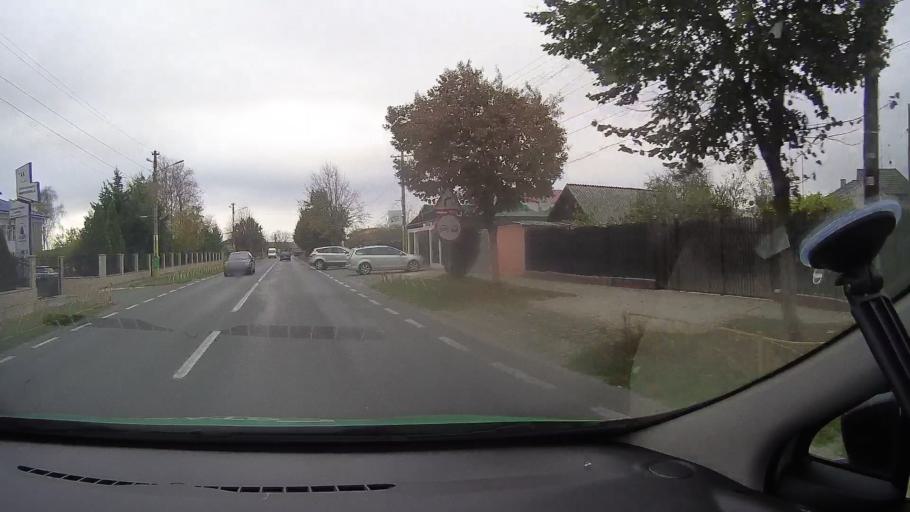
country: RO
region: Constanta
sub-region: Oras Murfatlar
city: Murfatlar
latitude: 44.1755
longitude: 28.4066
